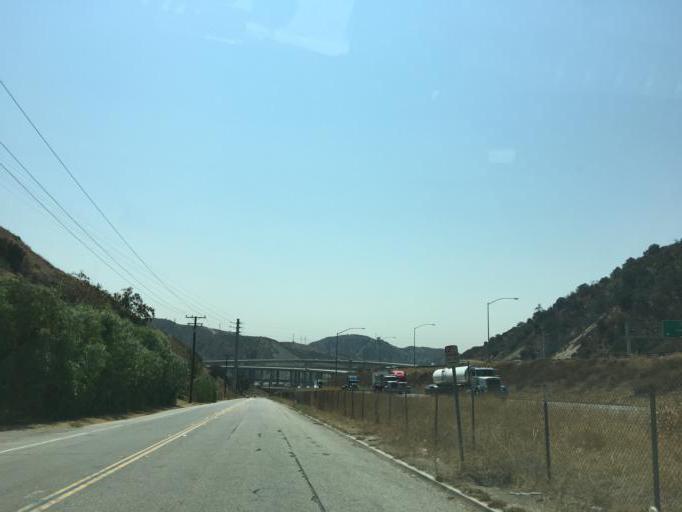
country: US
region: California
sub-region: Los Angeles County
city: Santa Clarita
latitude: 34.3387
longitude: -118.5151
